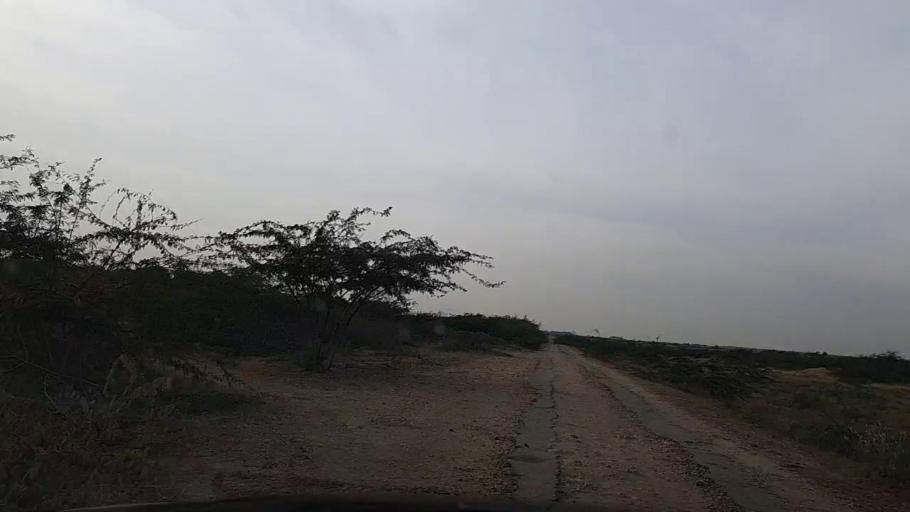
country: PK
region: Sindh
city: Gharo
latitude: 24.7915
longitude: 67.5476
